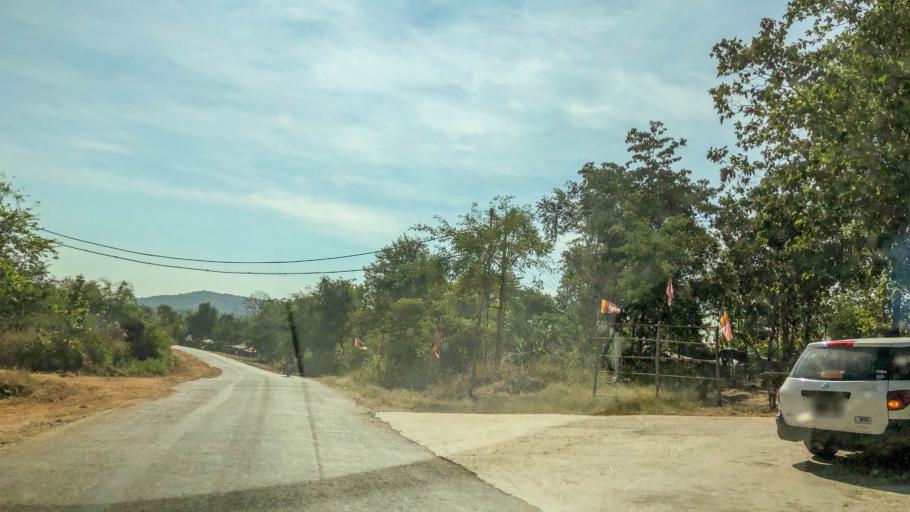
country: MM
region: Magway
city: Magway
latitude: 19.7613
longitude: 94.9389
